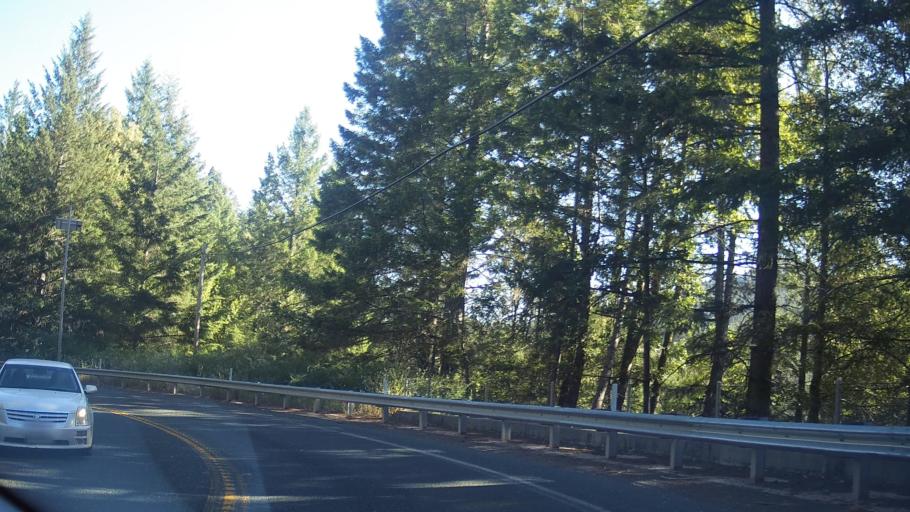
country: US
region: California
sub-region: Mendocino County
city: Brooktrails
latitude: 39.3974
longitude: -123.4539
